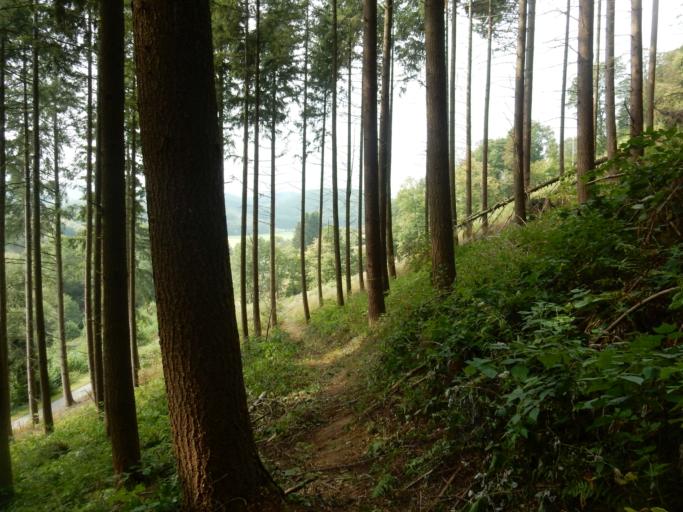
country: LU
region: Diekirch
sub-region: Canton de Wiltz
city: Winseler
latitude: 49.9658
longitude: 5.9085
